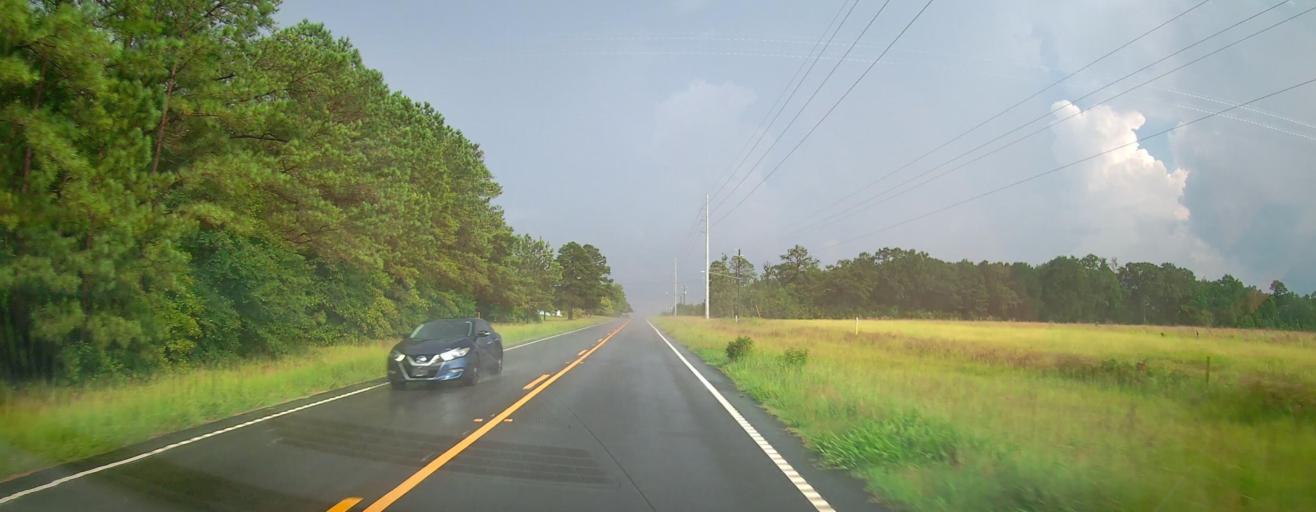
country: US
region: Georgia
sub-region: Twiggs County
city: Jeffersonville
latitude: 32.5963
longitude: -83.2341
